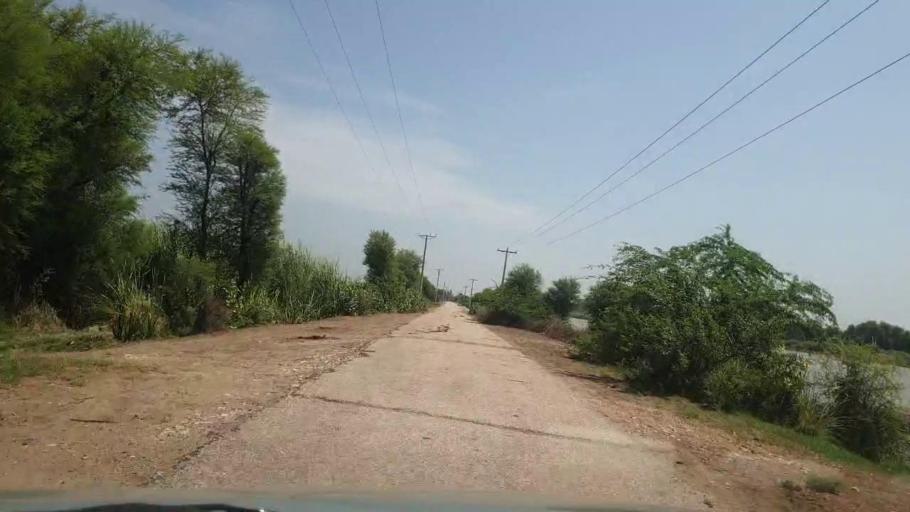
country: PK
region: Sindh
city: Bozdar
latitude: 27.1160
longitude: 68.9896
